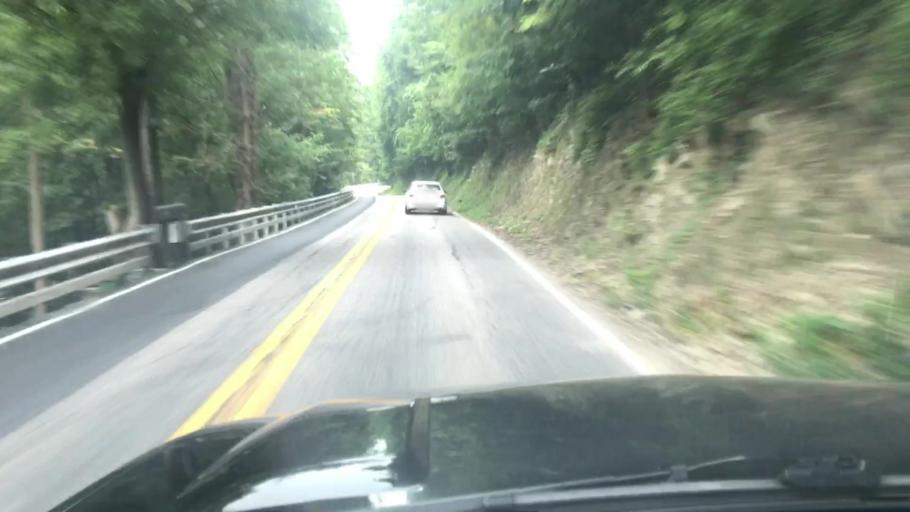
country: US
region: Pennsylvania
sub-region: Cumberland County
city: Shiremanstown
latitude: 40.2534
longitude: -76.9746
